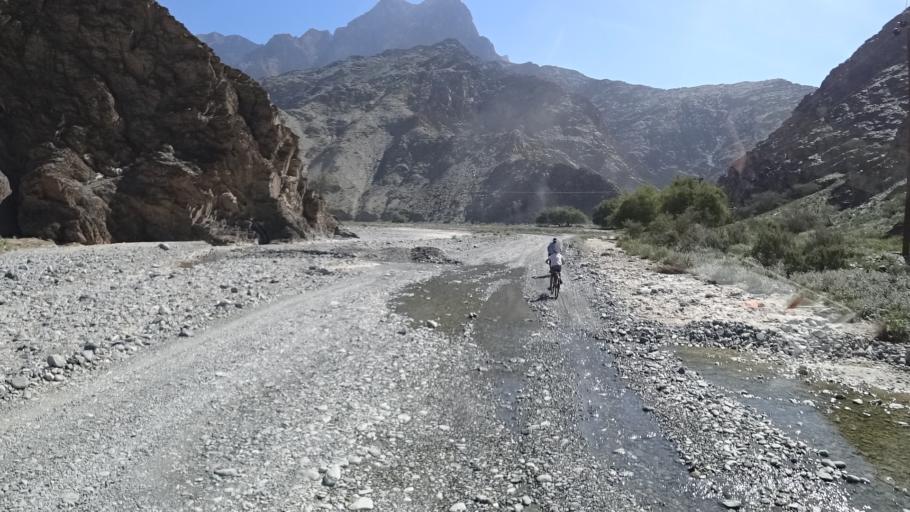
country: OM
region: Al Batinah
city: Bayt al `Awabi
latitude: 23.2589
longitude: 57.4394
